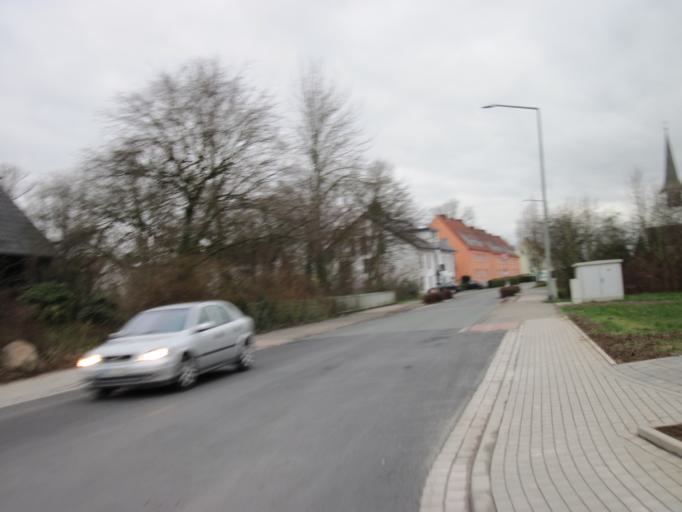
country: DE
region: North Rhine-Westphalia
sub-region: Regierungsbezirk Detmold
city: Salzkotten
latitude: 51.6669
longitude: 8.6074
